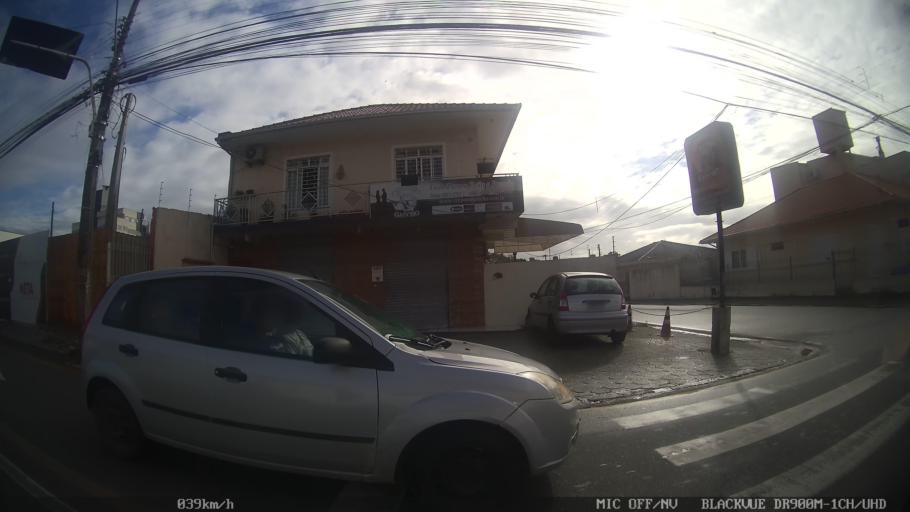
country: BR
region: Santa Catarina
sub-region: Sao Jose
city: Campinas
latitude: -27.6084
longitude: -48.6280
